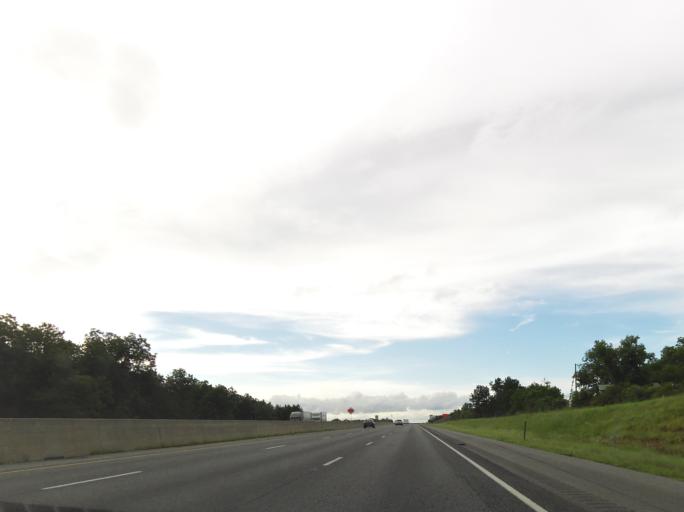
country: US
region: Georgia
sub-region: Tift County
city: Tifton
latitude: 31.5229
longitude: -83.5197
